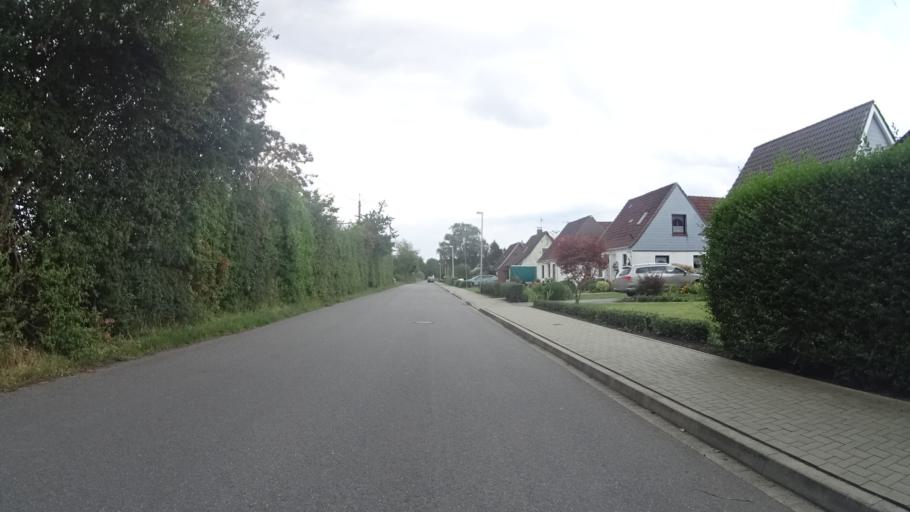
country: DE
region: Schleswig-Holstein
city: Gluckstadt
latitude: 53.7835
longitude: 9.4407
